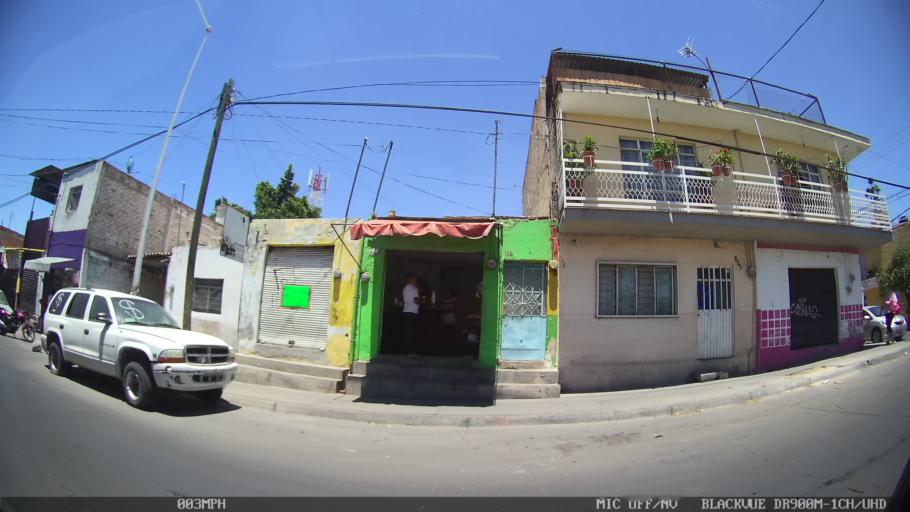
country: MX
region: Jalisco
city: Tlaquepaque
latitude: 20.6515
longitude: -103.2789
